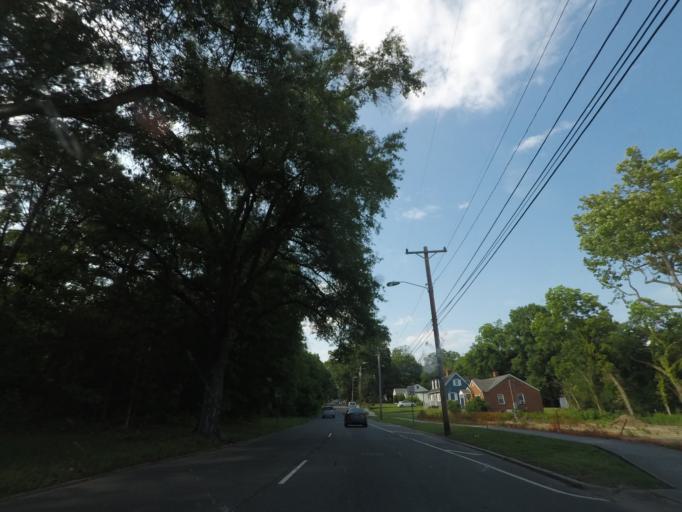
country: US
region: North Carolina
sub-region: Durham County
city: Durham
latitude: 35.9872
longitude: -78.9092
